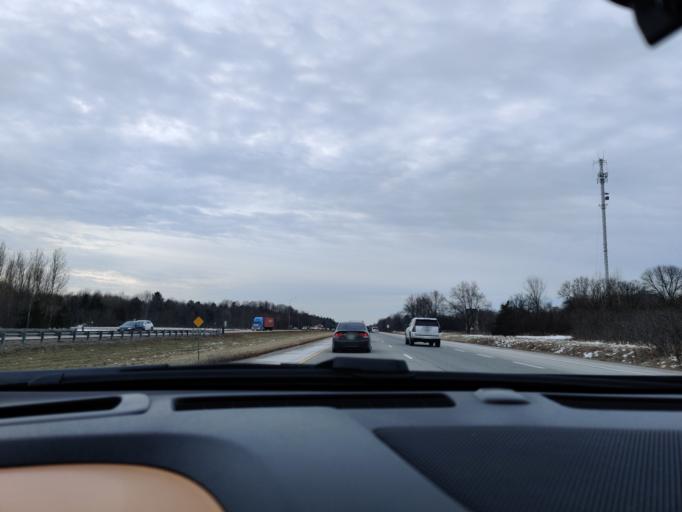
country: US
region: New York
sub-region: Jefferson County
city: Alexandria Bay
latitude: 44.4741
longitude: -75.8700
